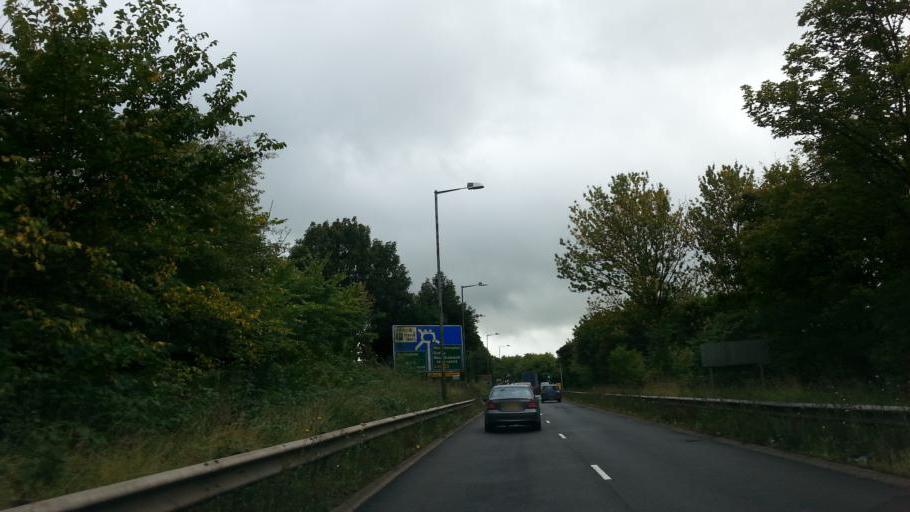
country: GB
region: England
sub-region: Sandwell
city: Smethwick
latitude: 52.5138
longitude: -1.9733
